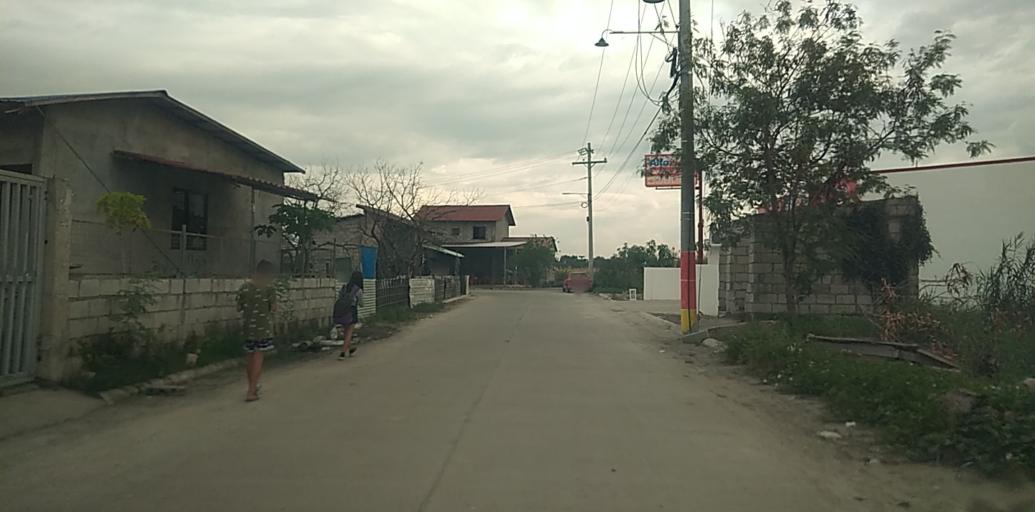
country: PH
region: Central Luzon
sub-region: Province of Pampanga
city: San Fernando
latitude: 15.0096
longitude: 120.7028
